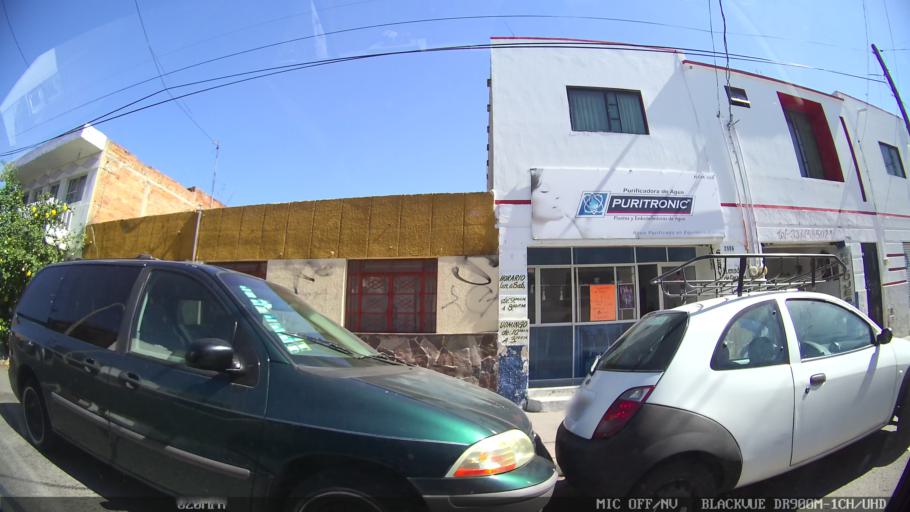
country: MX
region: Jalisco
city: Tlaquepaque
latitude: 20.6557
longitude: -103.2974
